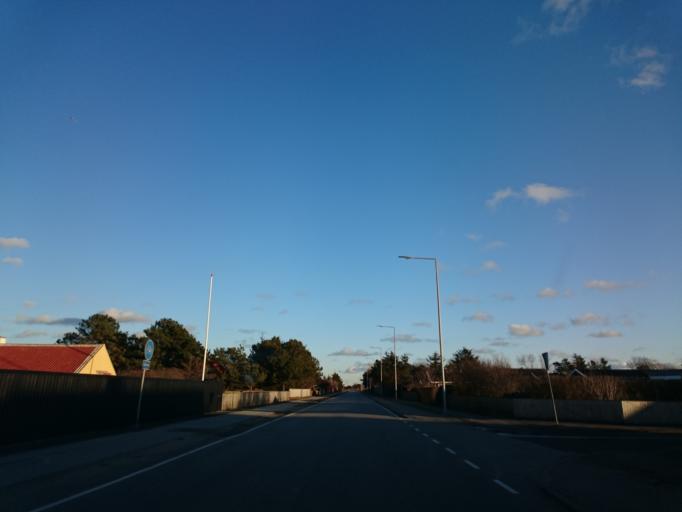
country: DK
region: North Denmark
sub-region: Frederikshavn Kommune
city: Skagen
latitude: 57.7274
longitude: 10.5423
